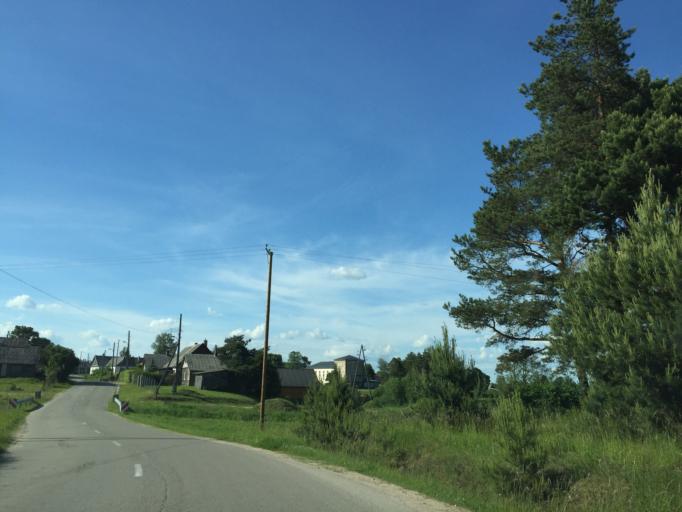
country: LV
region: Rezekne
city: Rezekne
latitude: 56.3450
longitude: 27.1674
